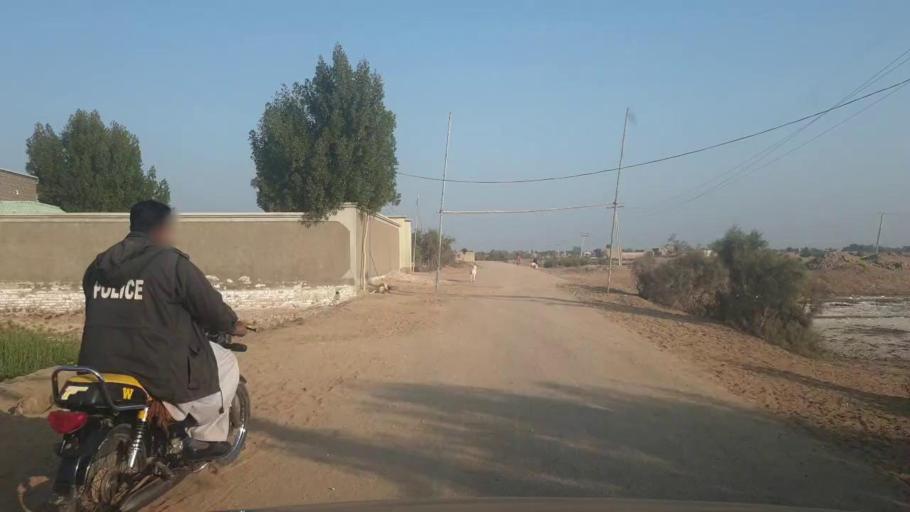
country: PK
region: Sindh
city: Sakrand
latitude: 26.0566
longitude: 68.3835
